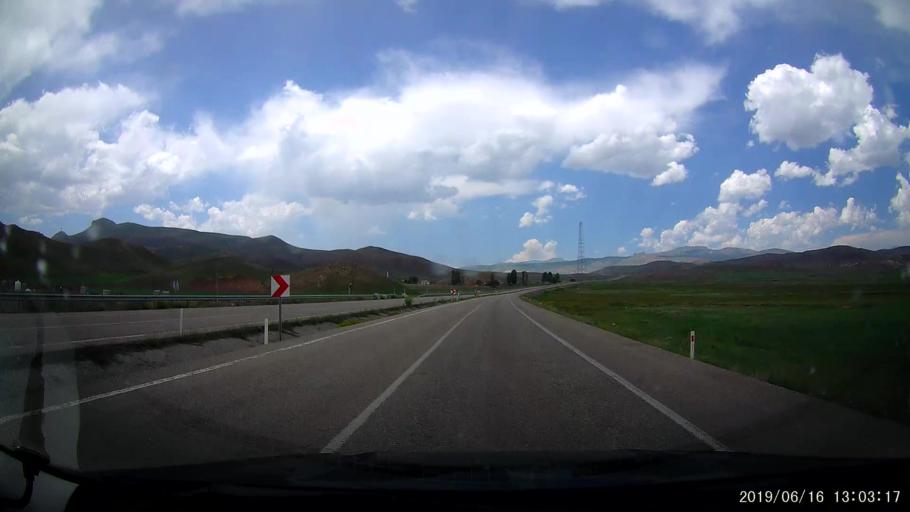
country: TR
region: Agri
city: Sulucem
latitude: 39.5800
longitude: 43.7936
